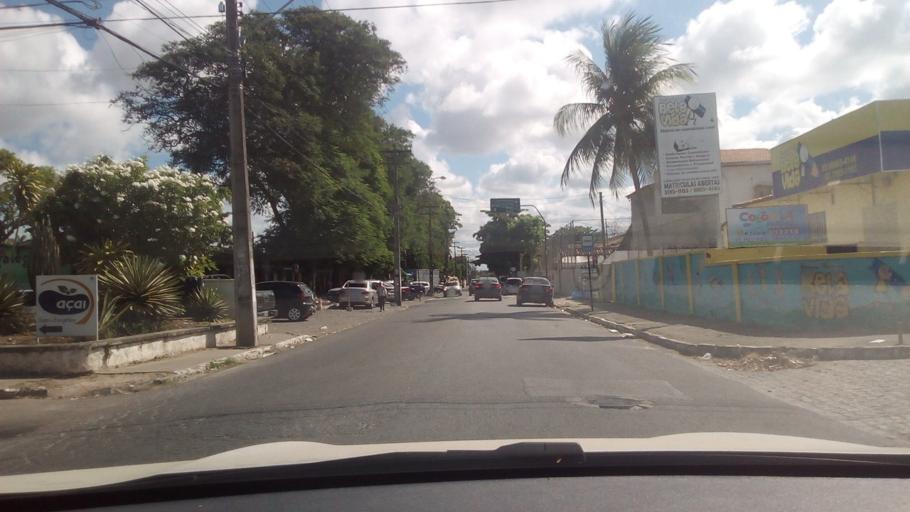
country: BR
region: Paraiba
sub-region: Joao Pessoa
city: Joao Pessoa
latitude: -7.1340
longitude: -34.8717
